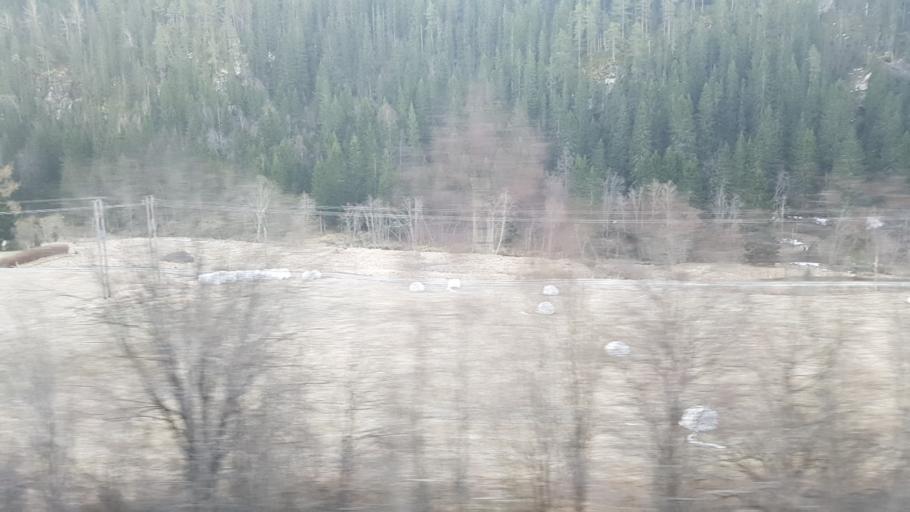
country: NO
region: Nord-Trondelag
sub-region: Stjordal
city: Stjordalshalsen
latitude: 63.5985
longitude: 11.0227
